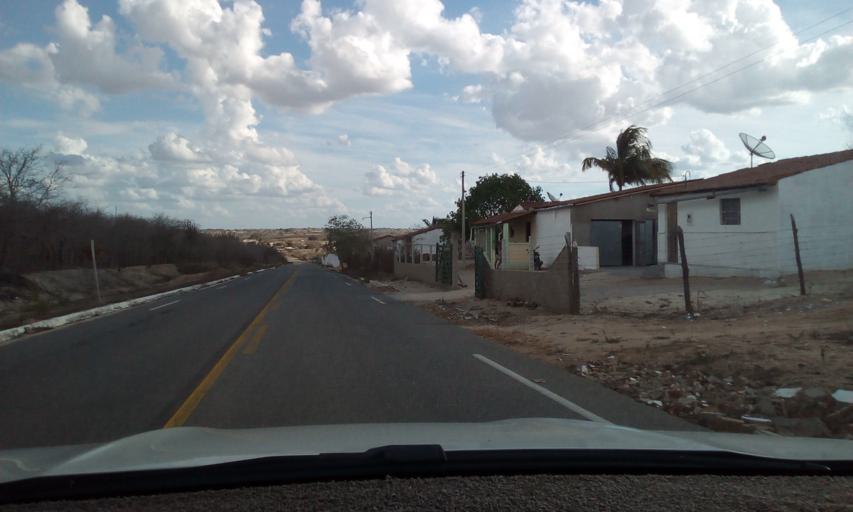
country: BR
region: Paraiba
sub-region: Soledade
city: Soledade
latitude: -6.8866
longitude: -36.3989
